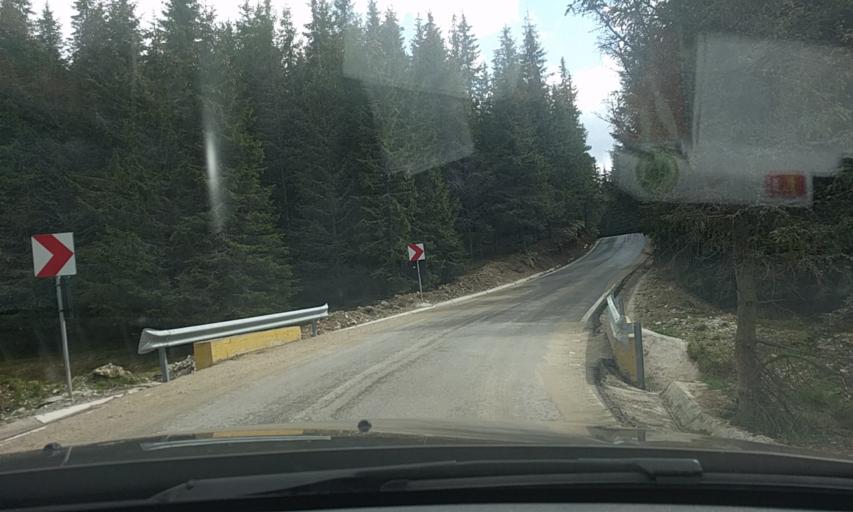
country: RO
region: Prahova
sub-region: Oras Busteni
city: Busteni
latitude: 45.3878
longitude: 25.4393
